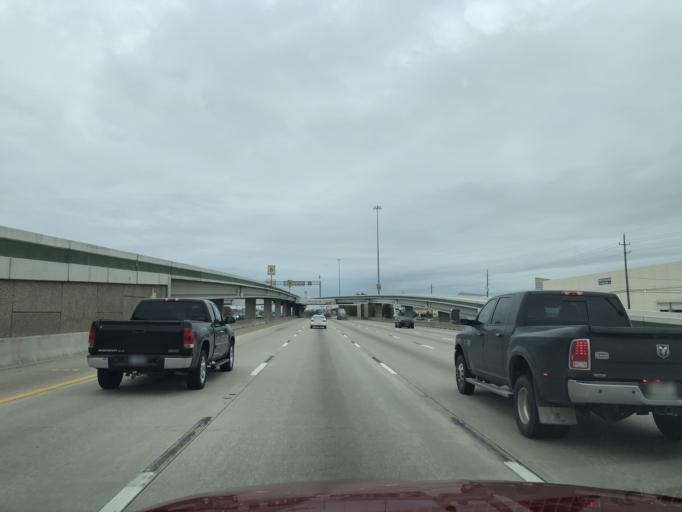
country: US
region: Texas
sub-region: Harris County
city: Spring
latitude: 30.0148
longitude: -95.4284
